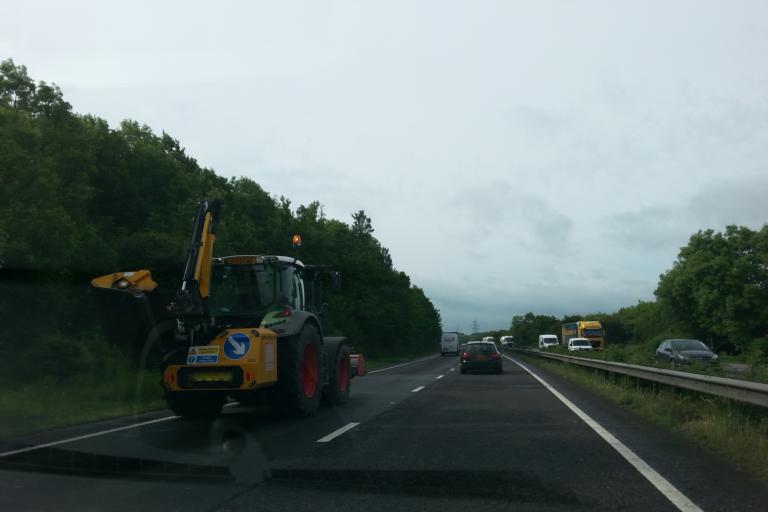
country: GB
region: England
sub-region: Lincolnshire
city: Great Gonerby
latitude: 52.9370
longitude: -0.6851
